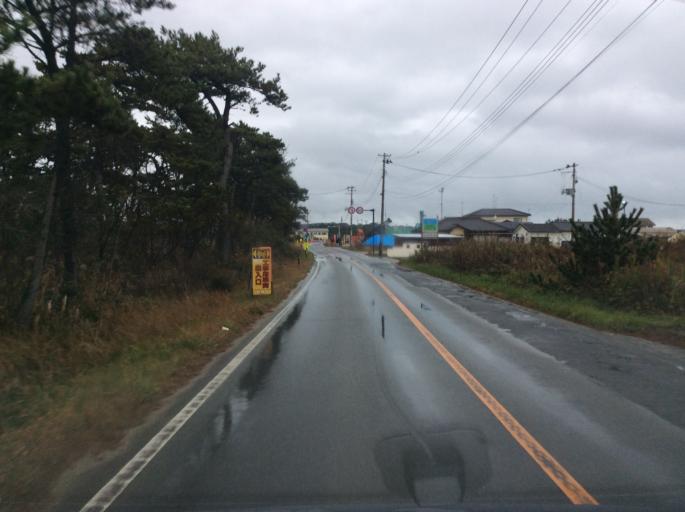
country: JP
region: Fukushima
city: Iwaki
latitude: 37.0874
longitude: 140.9815
